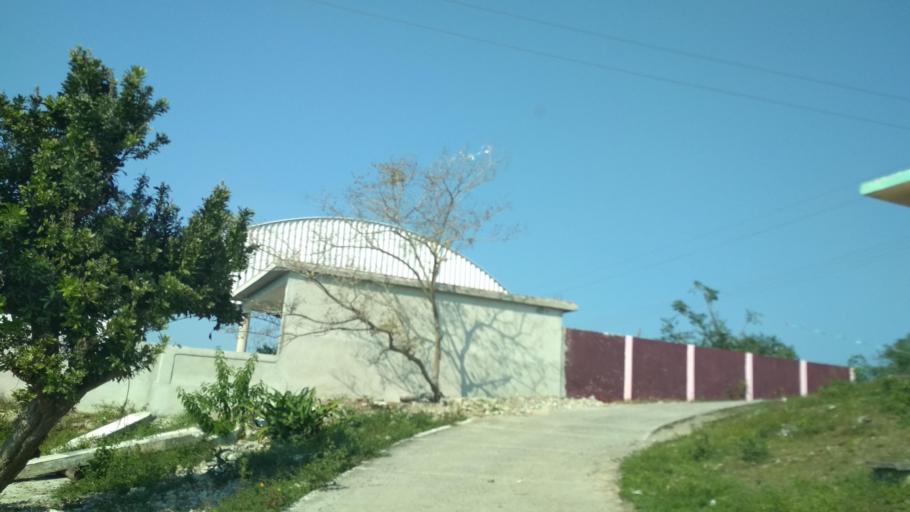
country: MX
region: Veracruz
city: Agua Dulce
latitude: 20.3881
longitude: -97.2133
